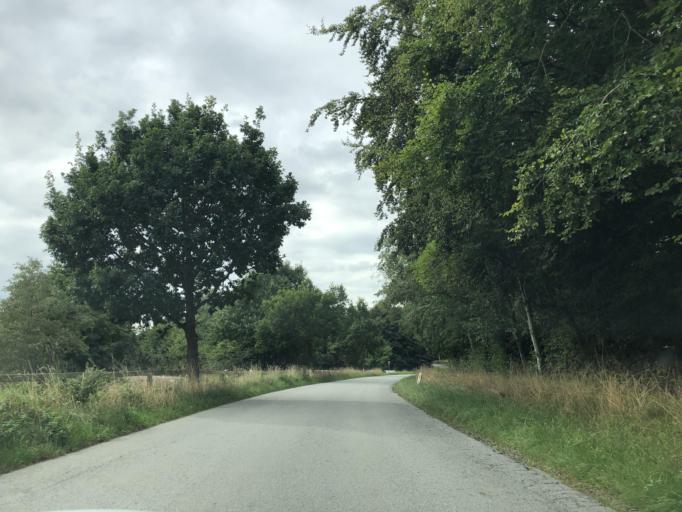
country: DK
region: North Denmark
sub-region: Alborg Kommune
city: Svenstrup
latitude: 56.9353
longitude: 9.8062
